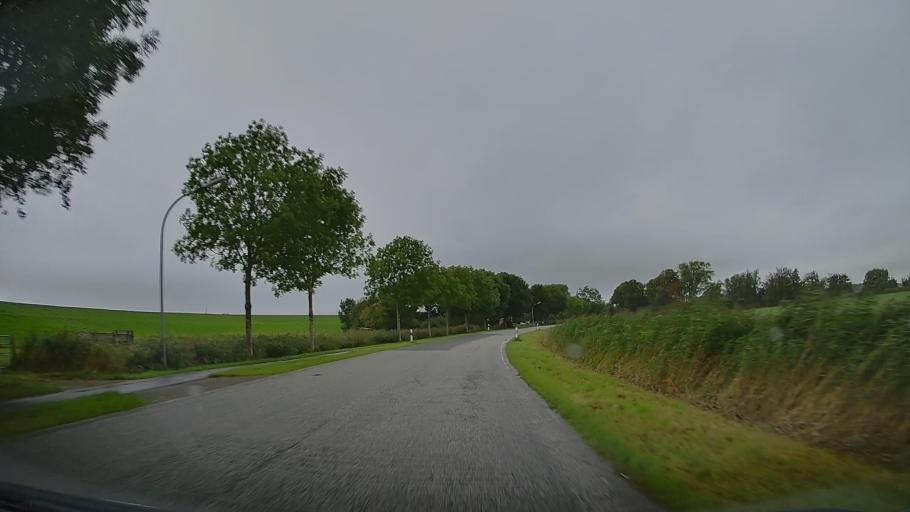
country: DE
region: Schleswig-Holstein
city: Sankt Margarethen
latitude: 53.8818
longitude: 9.2596
